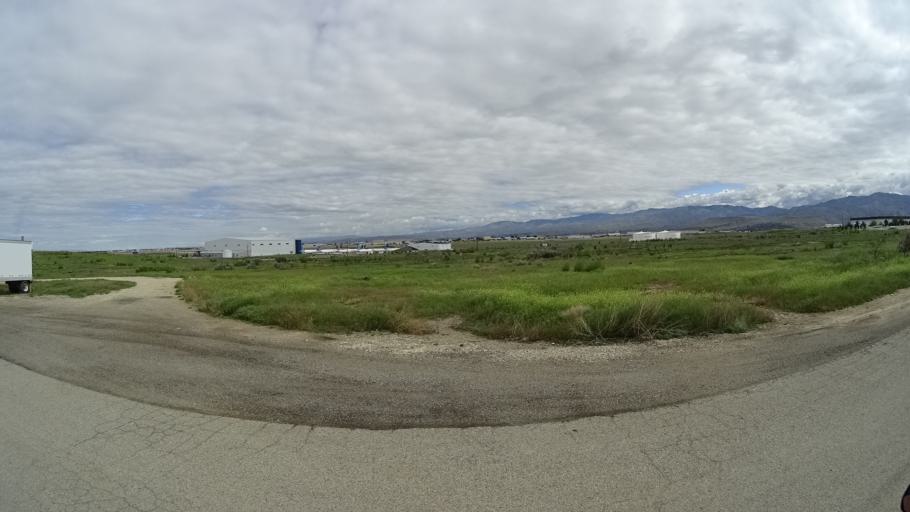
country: US
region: Idaho
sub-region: Ada County
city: Boise
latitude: 43.5460
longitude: -116.1975
